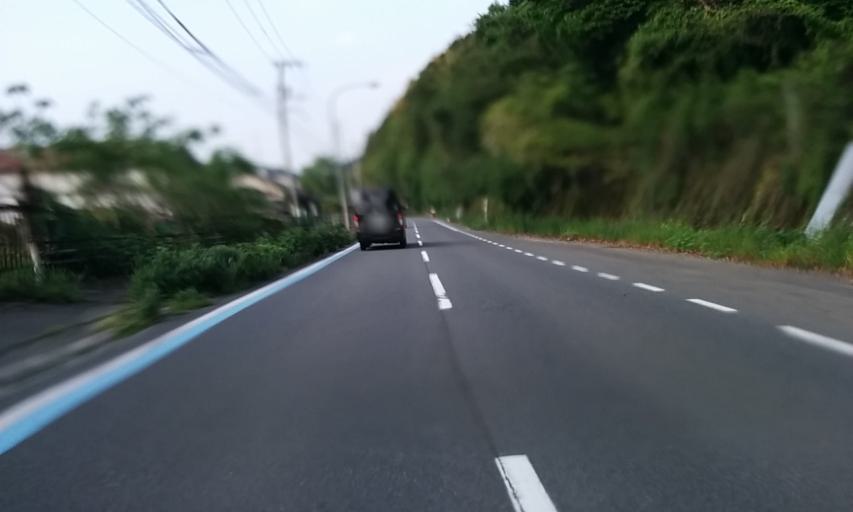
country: JP
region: Ehime
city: Saijo
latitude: 33.8794
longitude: 133.1763
